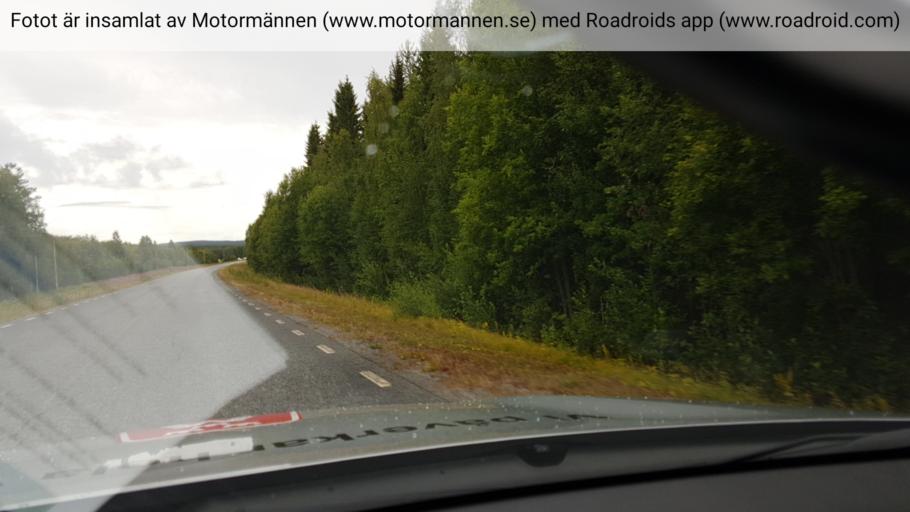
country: SE
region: Norrbotten
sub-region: Bodens Kommun
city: Boden
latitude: 65.8497
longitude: 21.4479
